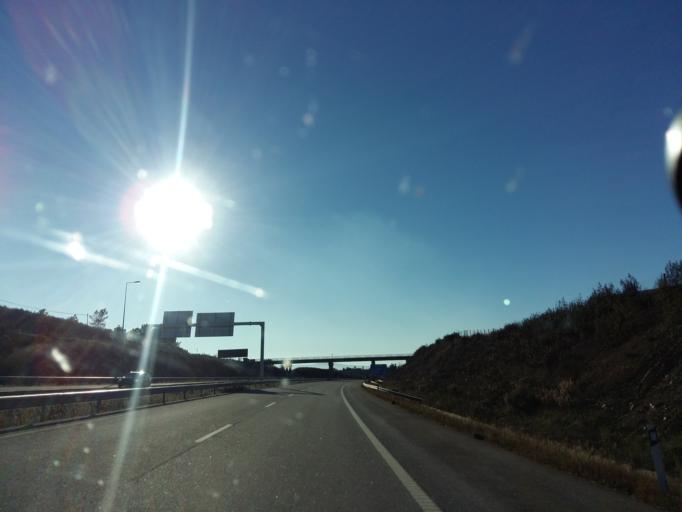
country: PT
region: Castelo Branco
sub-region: Castelo Branco
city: Castelo Branco
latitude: 39.7573
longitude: -7.6101
